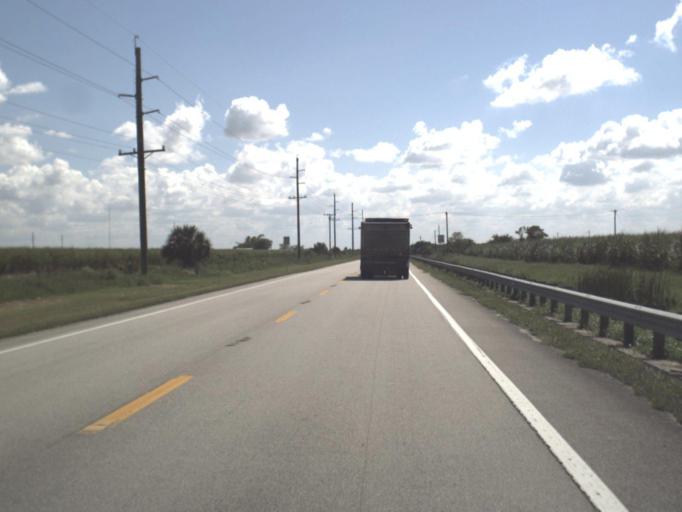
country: US
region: Florida
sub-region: Glades County
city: Moore Haven
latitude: 26.8561
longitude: -81.1228
